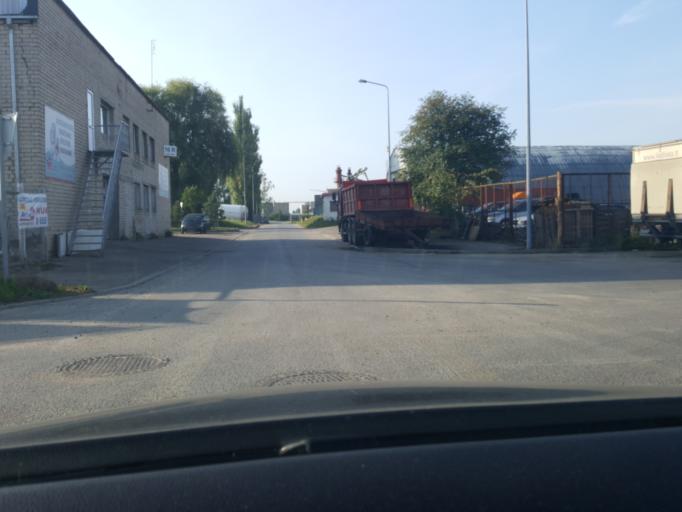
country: LT
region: Alytaus apskritis
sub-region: Alytus
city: Alytus
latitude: 54.4356
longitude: 24.0236
